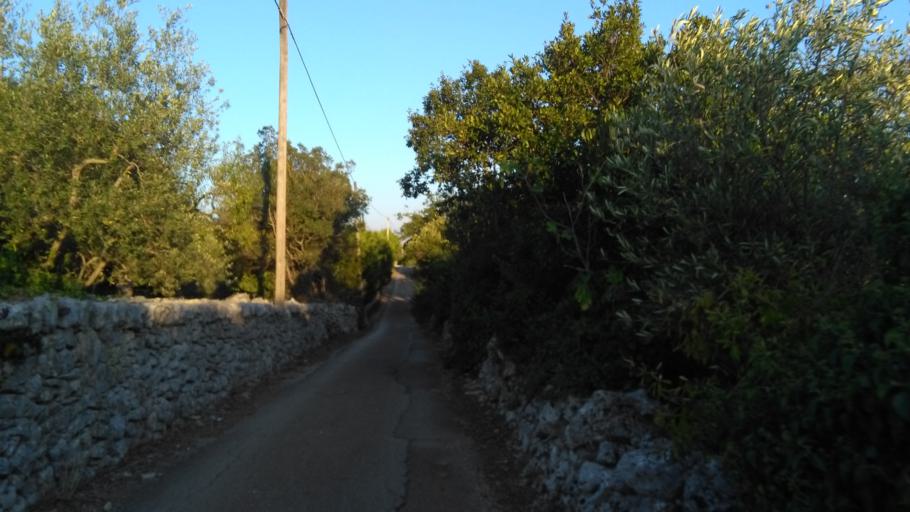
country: IT
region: Apulia
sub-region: Provincia di Bari
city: Putignano
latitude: 40.8245
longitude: 17.0976
